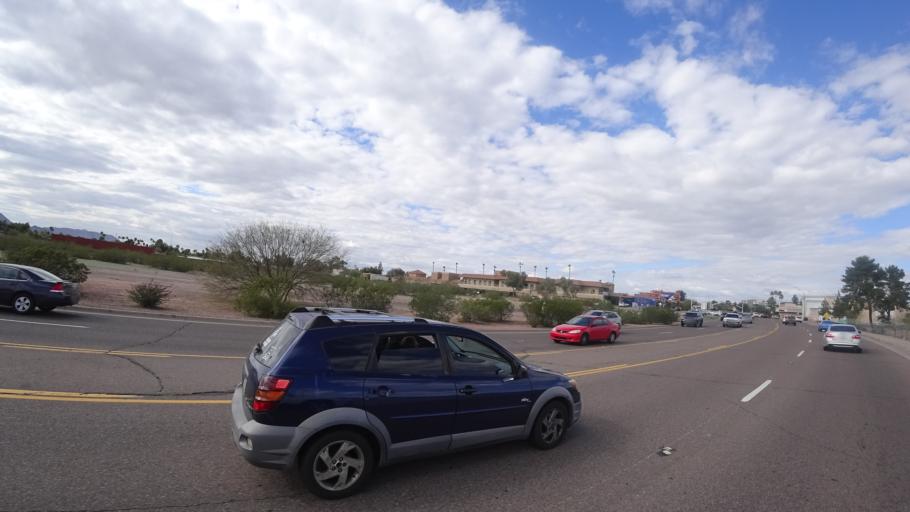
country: US
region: Arizona
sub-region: Maricopa County
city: Scottsdale
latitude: 33.5668
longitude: -111.8871
